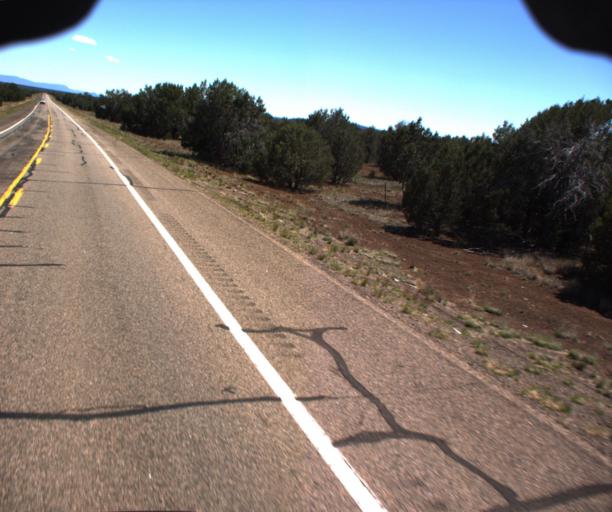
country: US
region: Arizona
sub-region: Yavapai County
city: Paulden
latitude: 35.1622
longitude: -112.4570
